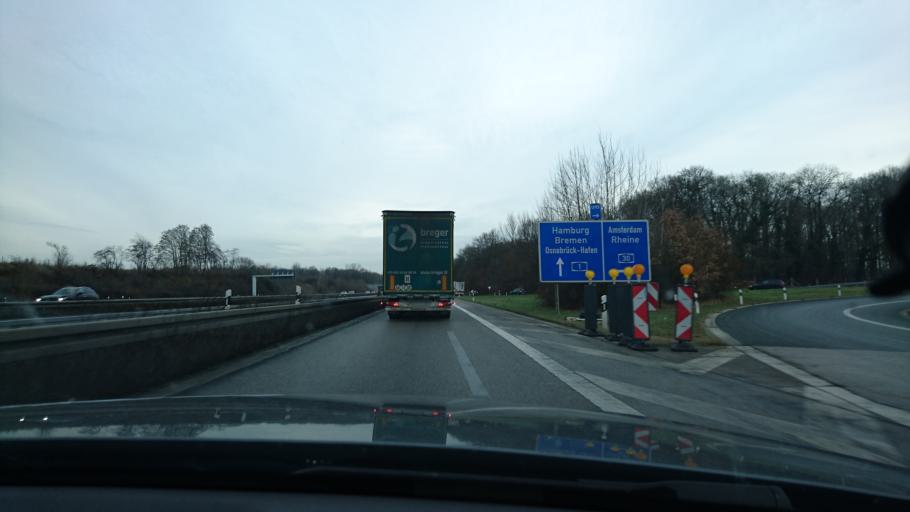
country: DE
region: North Rhine-Westphalia
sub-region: Regierungsbezirk Munster
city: Lotte
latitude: 52.2690
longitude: 7.9277
